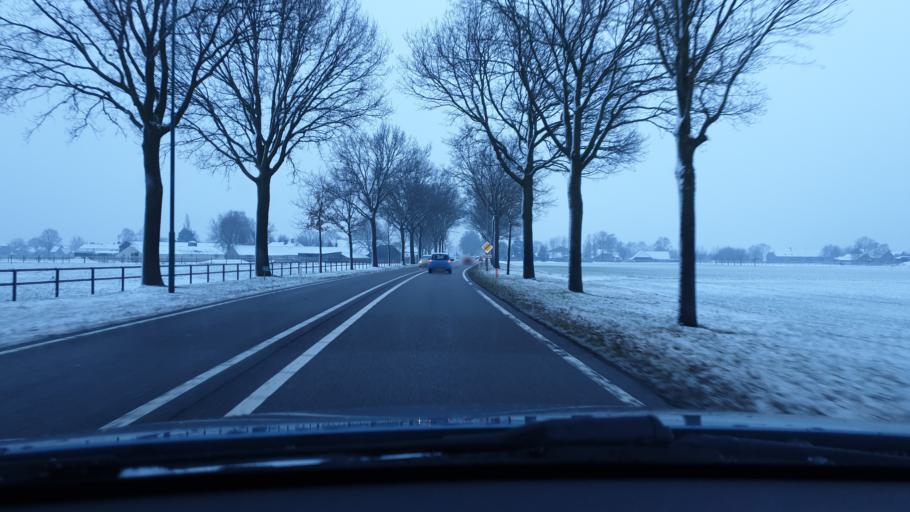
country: NL
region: North Brabant
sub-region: Gemeente Landerd
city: Zeeland
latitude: 51.7106
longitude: 5.6690
